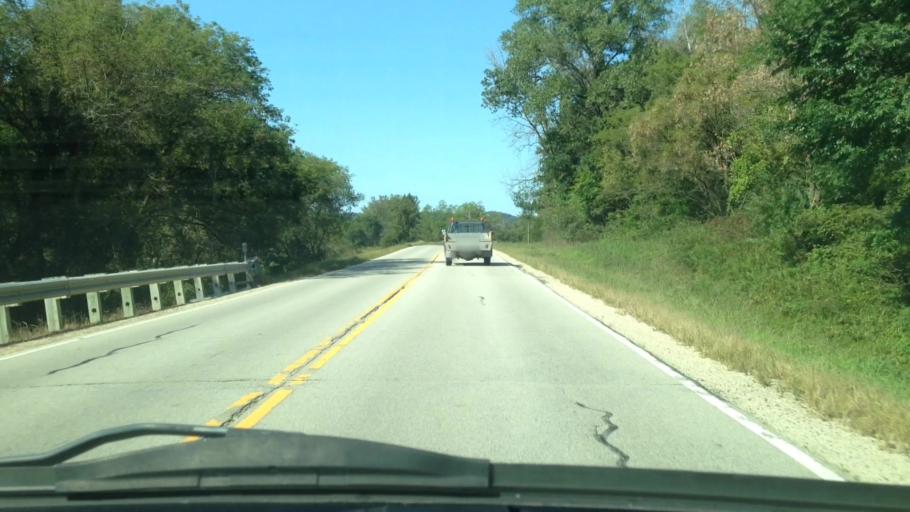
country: US
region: Minnesota
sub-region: Fillmore County
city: Rushford
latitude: 43.7686
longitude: -91.7636
